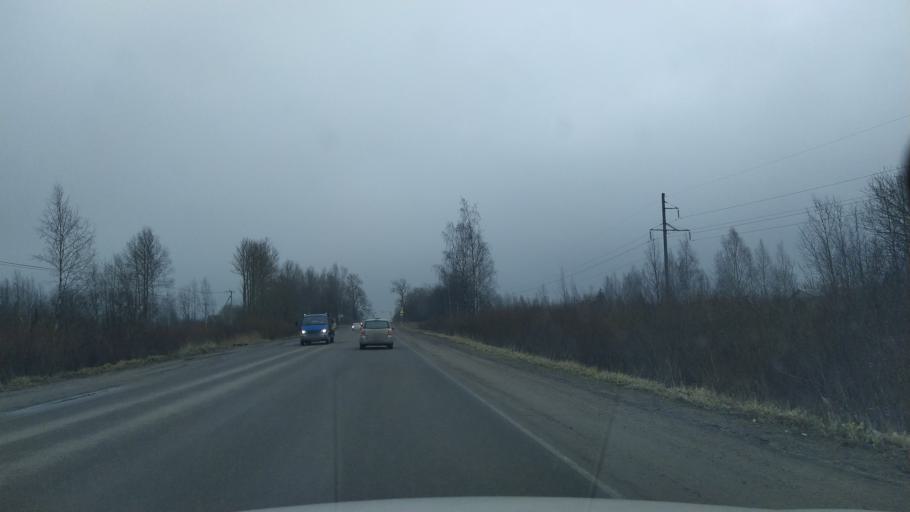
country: RU
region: St.-Petersburg
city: Gorelovo
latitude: 59.7301
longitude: 30.1483
